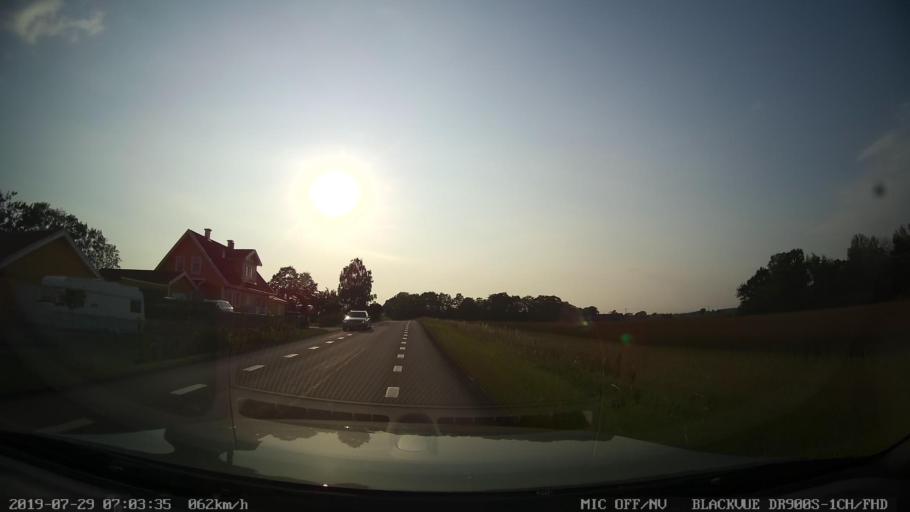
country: SE
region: Skane
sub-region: Helsingborg
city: Odakra
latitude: 56.1046
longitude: 12.7301
